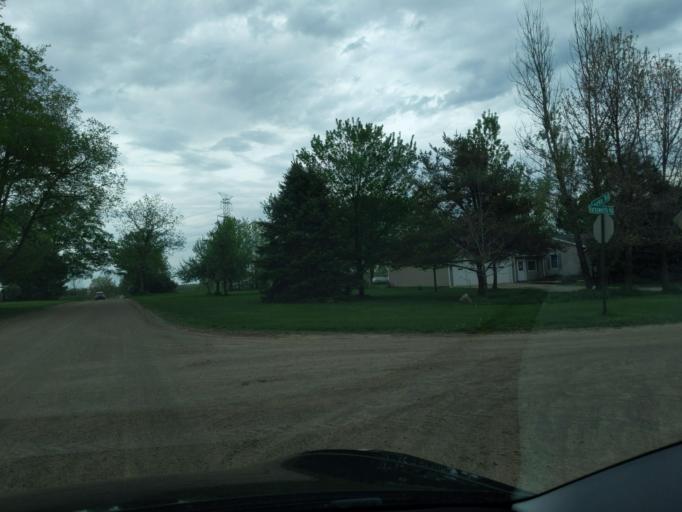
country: US
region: Michigan
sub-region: Ingham County
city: Stockbridge
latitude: 42.4164
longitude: -84.1363
